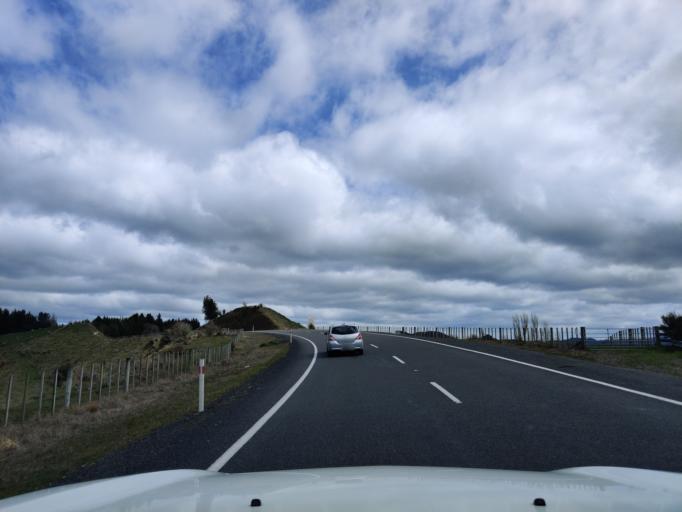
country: NZ
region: Manawatu-Wanganui
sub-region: Wanganui District
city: Wanganui
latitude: -39.7858
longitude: 175.2204
